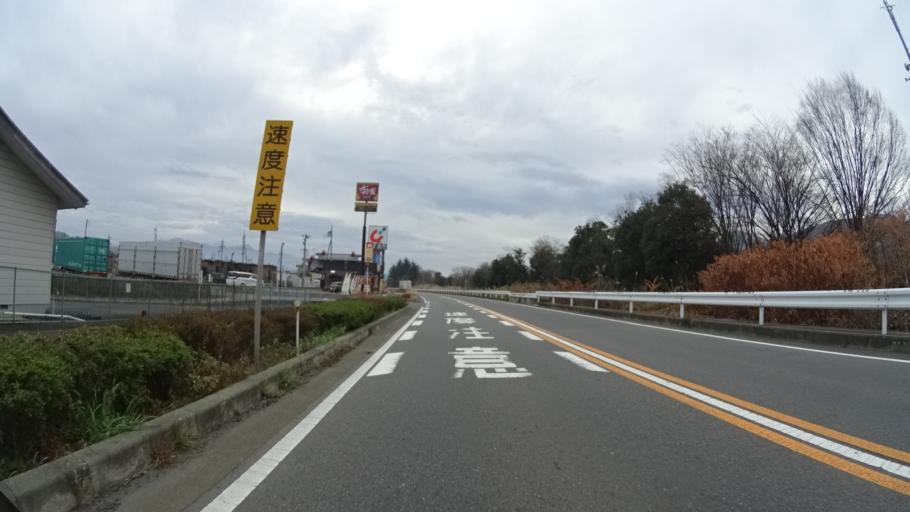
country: JP
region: Gunma
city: Numata
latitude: 36.6523
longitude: 139.0227
